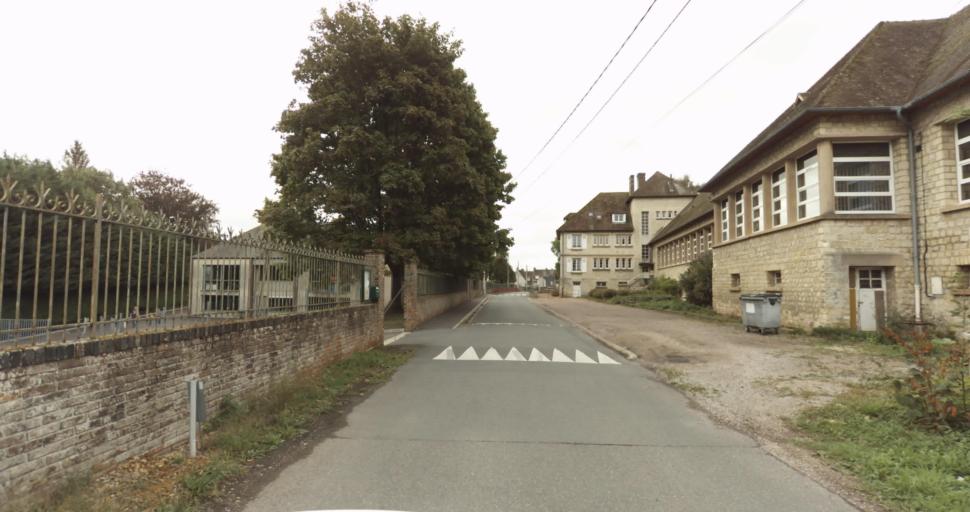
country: FR
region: Lower Normandy
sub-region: Departement de l'Orne
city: Vimoutiers
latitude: 48.9301
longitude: 0.1940
